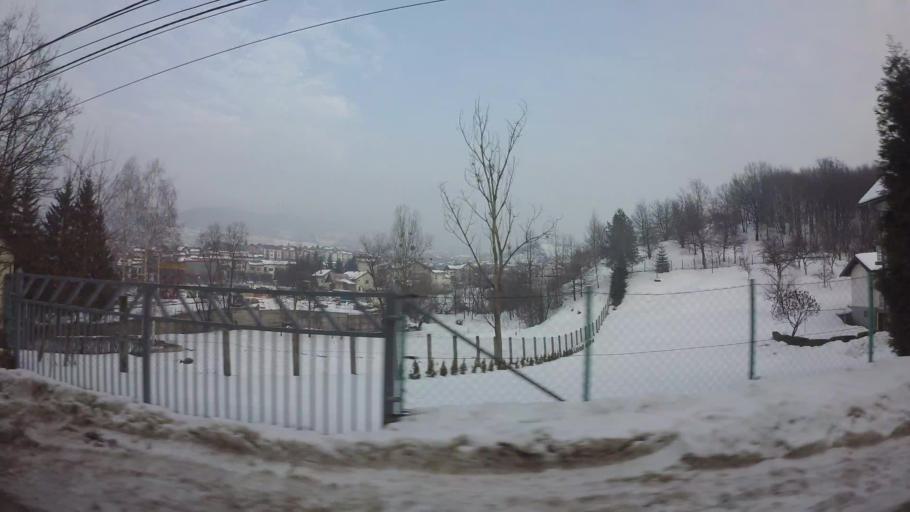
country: BA
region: Federation of Bosnia and Herzegovina
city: Hotonj
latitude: 43.8933
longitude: 18.3708
